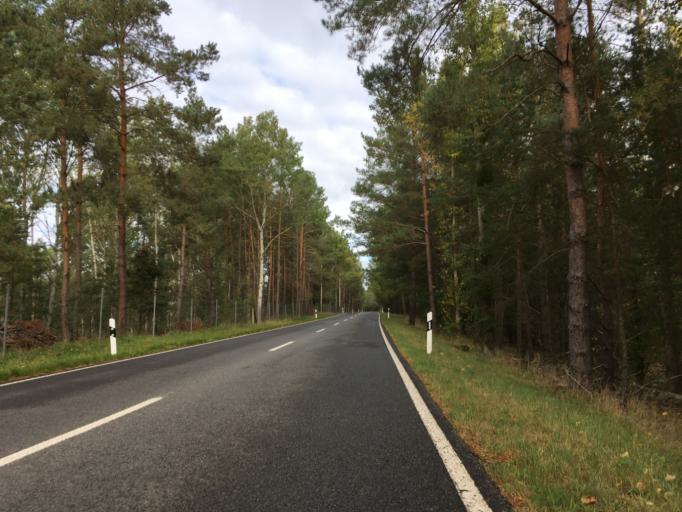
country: PL
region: West Pomeranian Voivodeship
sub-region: Powiat gryfinski
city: Cedynia
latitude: 52.8947
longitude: 14.1304
